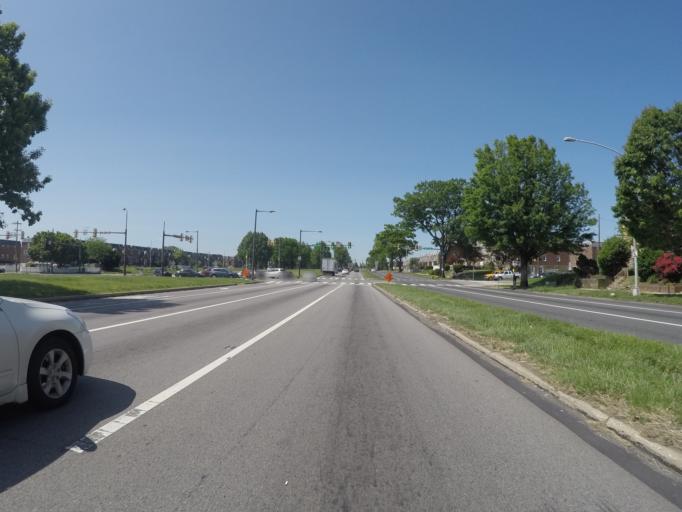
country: US
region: New Jersey
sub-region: Burlington County
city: Palmyra
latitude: 40.0412
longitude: -75.0582
